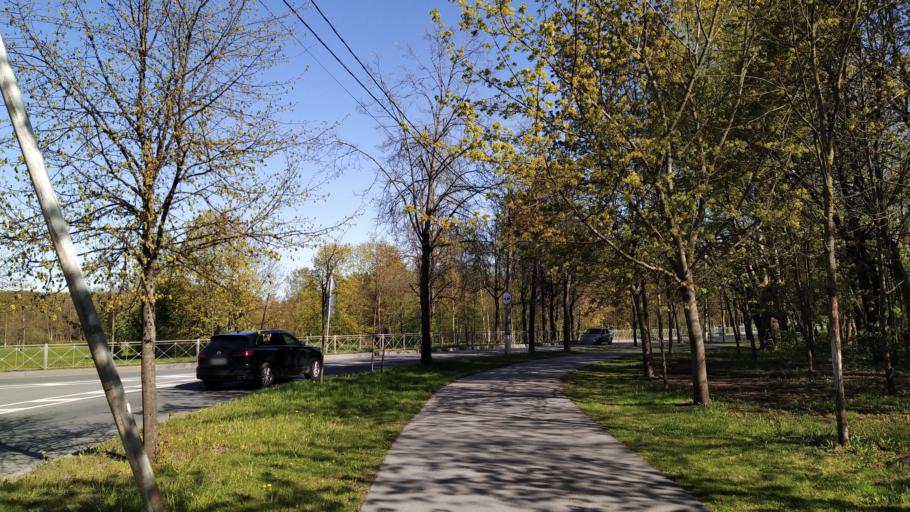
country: RU
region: St.-Petersburg
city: Pavlovsk
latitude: 59.7021
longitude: 30.4204
